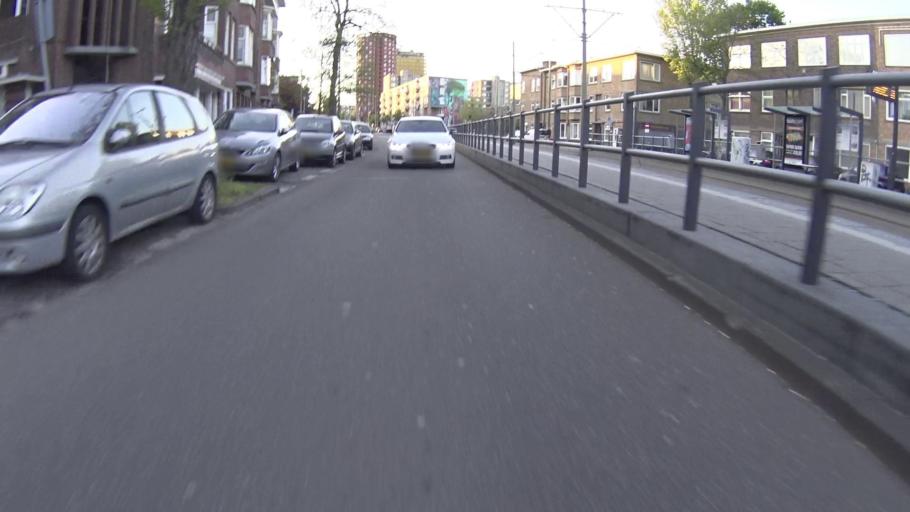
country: NL
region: South Holland
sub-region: Gemeente Rijswijk
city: Rijswijk
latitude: 52.0628
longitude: 4.3252
